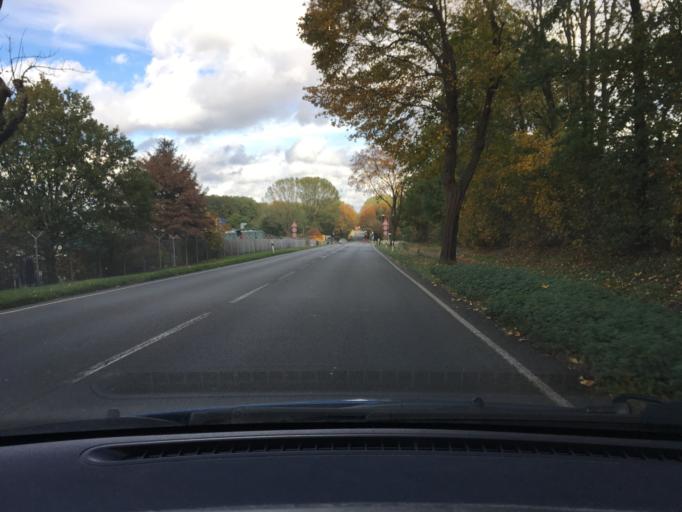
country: DE
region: Lower Saxony
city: Buchholz in der Nordheide
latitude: 53.3384
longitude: 9.8451
